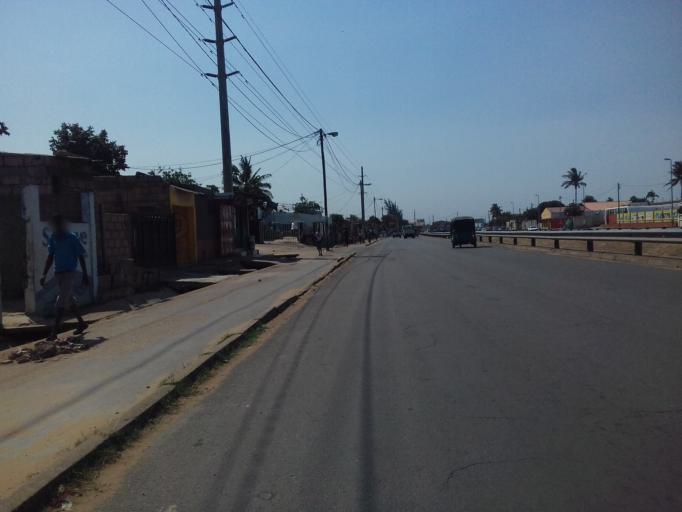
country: MZ
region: Maputo City
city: Maputo
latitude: -25.9456
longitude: 32.5755
